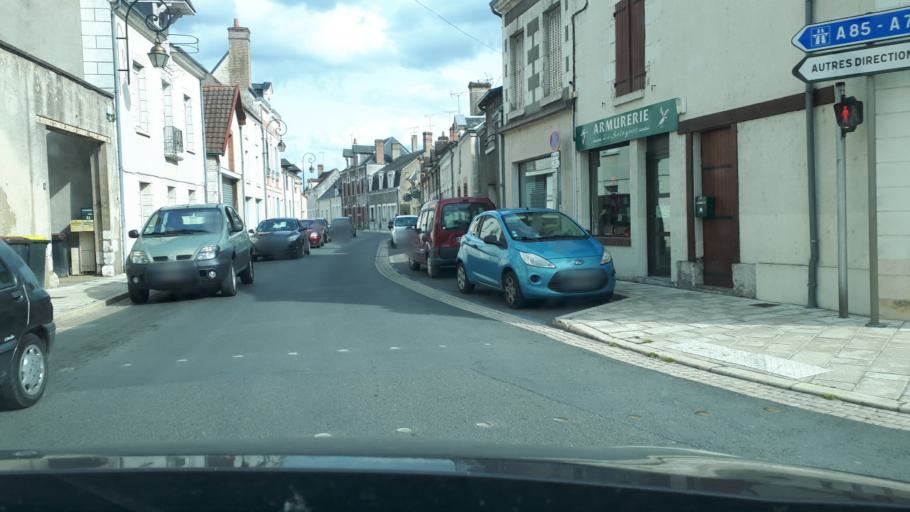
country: FR
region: Centre
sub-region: Departement du Loir-et-Cher
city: Romorantin-Lanthenay
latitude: 47.3546
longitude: 1.7426
